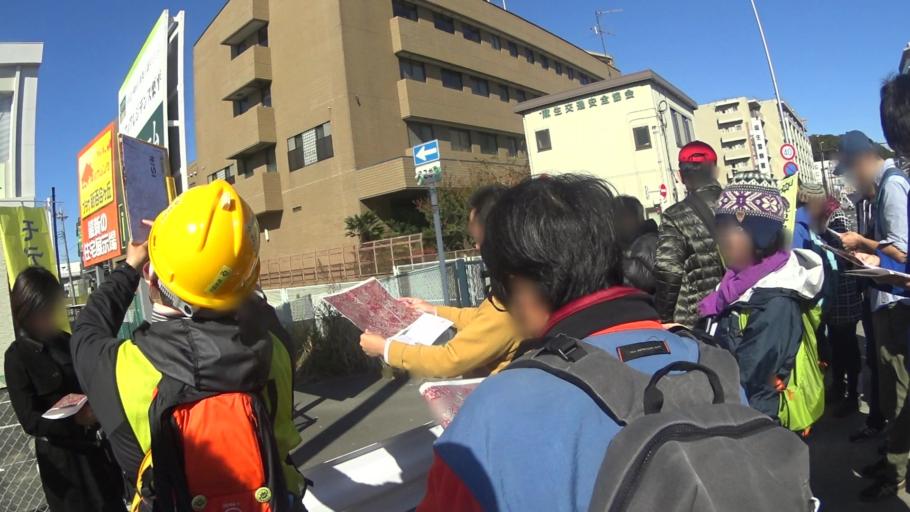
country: JP
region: Tokyo
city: Chofugaoka
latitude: 35.6054
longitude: 139.5001
